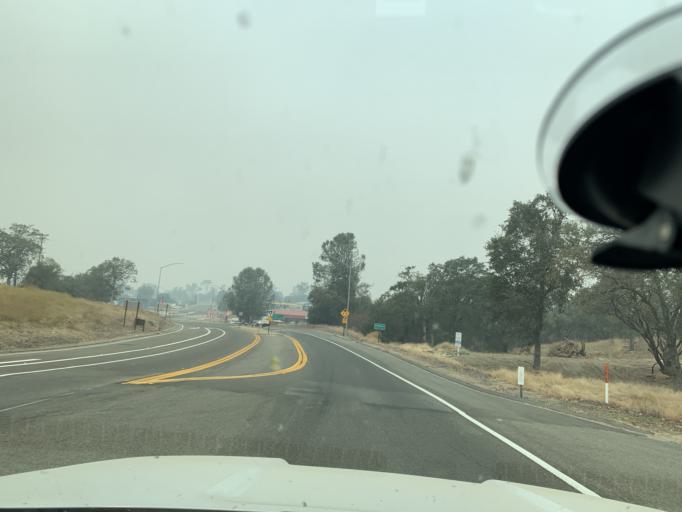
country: US
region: California
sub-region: Fresno County
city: Auberry
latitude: 37.0367
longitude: -119.5116
